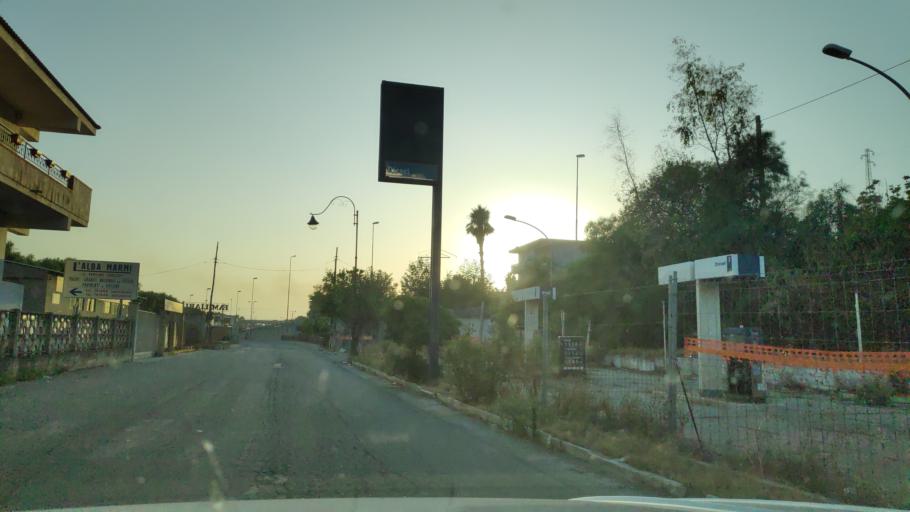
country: IT
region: Calabria
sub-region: Provincia di Reggio Calabria
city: Bova Marina
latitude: 37.9289
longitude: 15.9059
